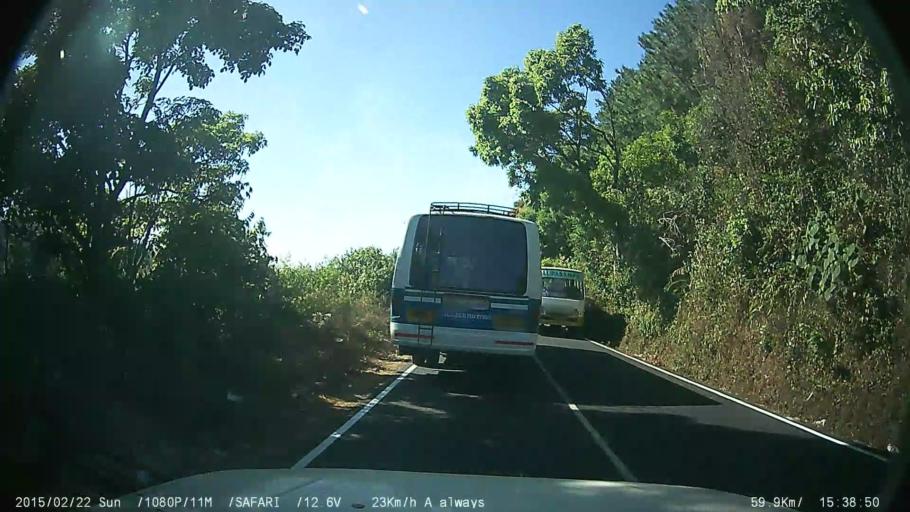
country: IN
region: Kerala
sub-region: Kottayam
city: Erattupetta
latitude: 9.5619
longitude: 76.9805
